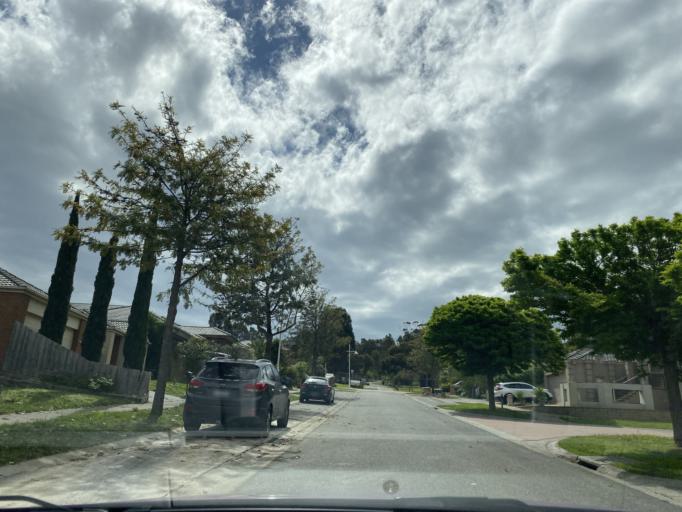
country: AU
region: Victoria
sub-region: Whittlesea
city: Epping
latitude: -37.6321
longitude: 145.0616
